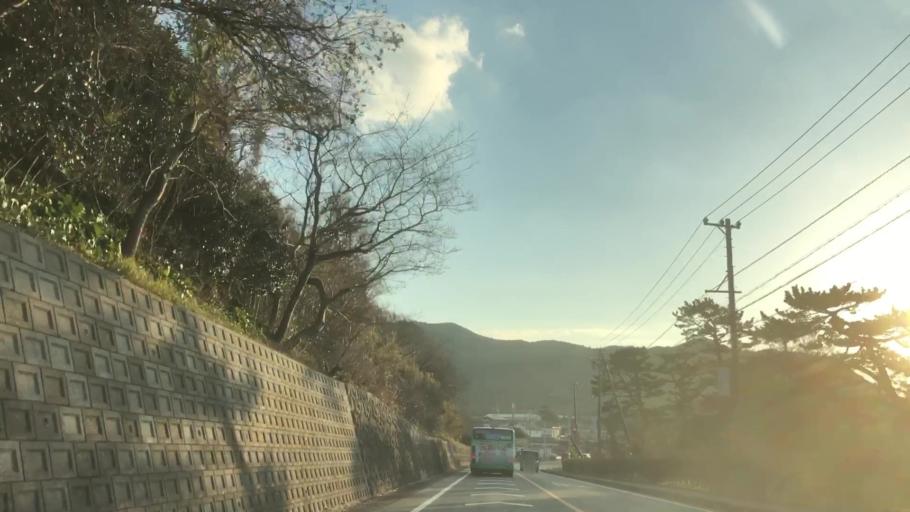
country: JP
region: Aichi
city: Tahara
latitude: 34.6608
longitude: 137.1791
